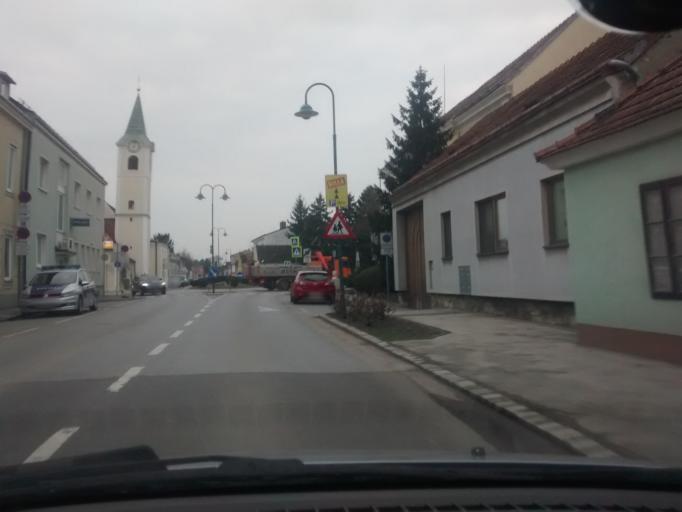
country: AT
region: Lower Austria
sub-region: Politischer Bezirk Wien-Umgebung
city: Gramatneusiedl
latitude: 48.0295
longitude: 16.4903
